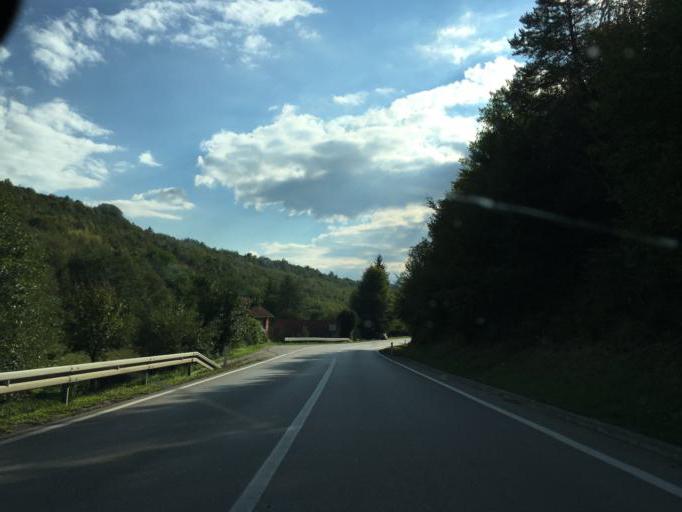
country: BA
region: Federation of Bosnia and Herzegovina
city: Bugojno
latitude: 44.0739
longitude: 17.5010
